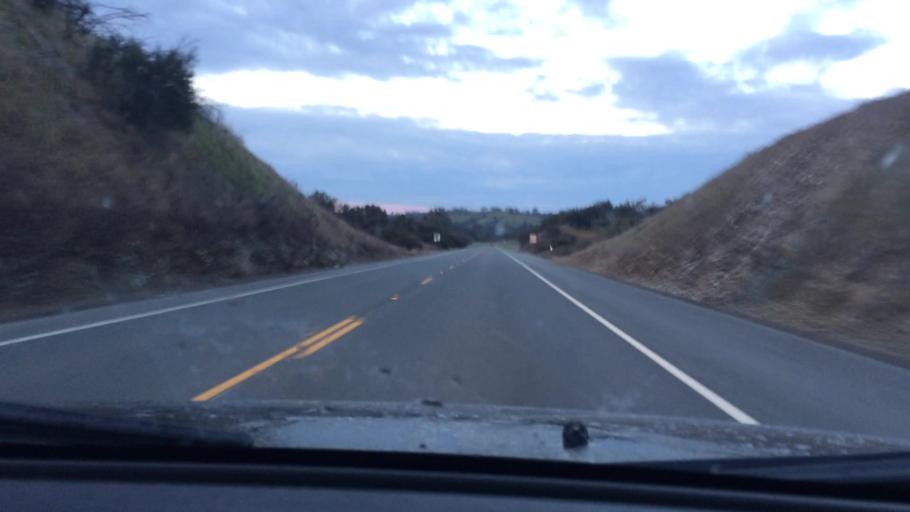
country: US
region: California
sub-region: Amador County
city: Ione
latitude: 38.3958
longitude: -120.8981
